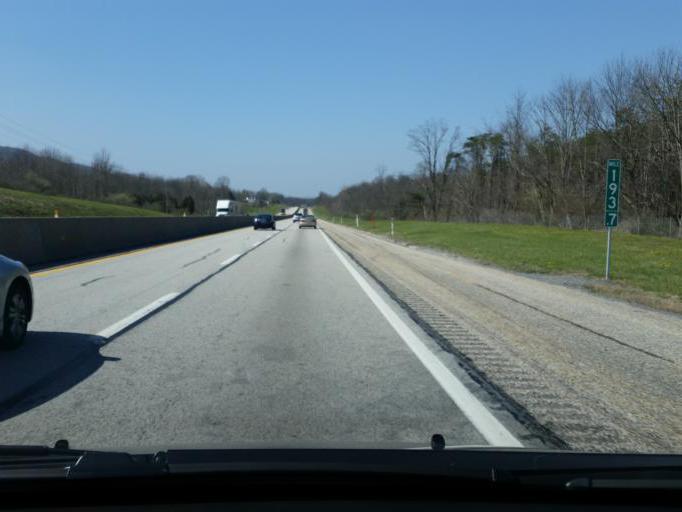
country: US
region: Pennsylvania
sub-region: Franklin County
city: Doylestown
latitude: 40.1373
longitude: -77.7336
